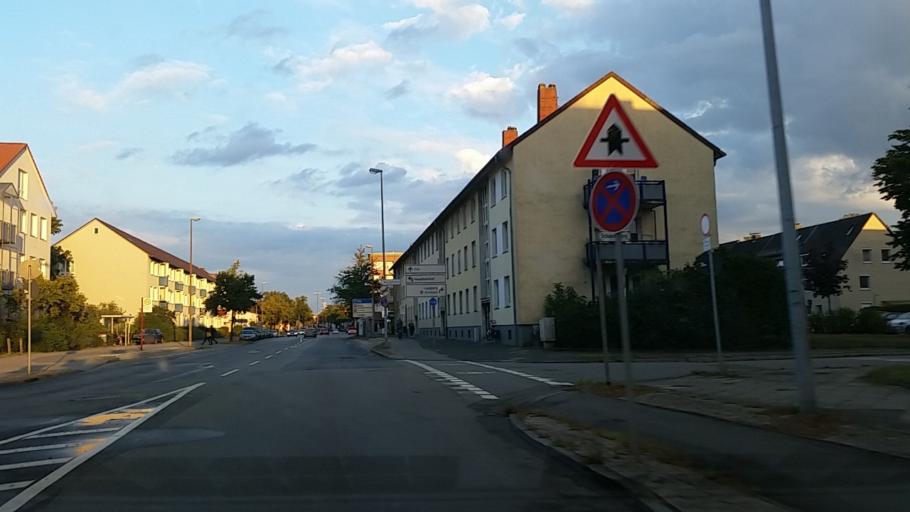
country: DE
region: Lower Saxony
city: Wolfsburg
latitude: 52.4241
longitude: 10.7733
